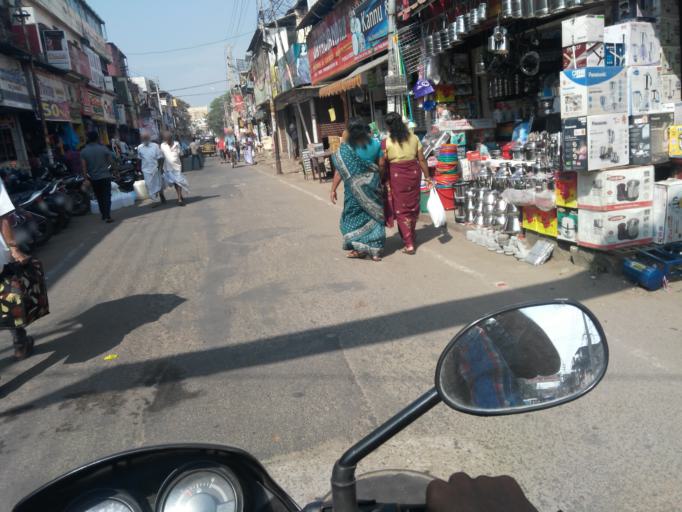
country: IN
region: Kerala
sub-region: Thiruvananthapuram
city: Thiruvananthapuram
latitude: 8.4828
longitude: 76.9498
